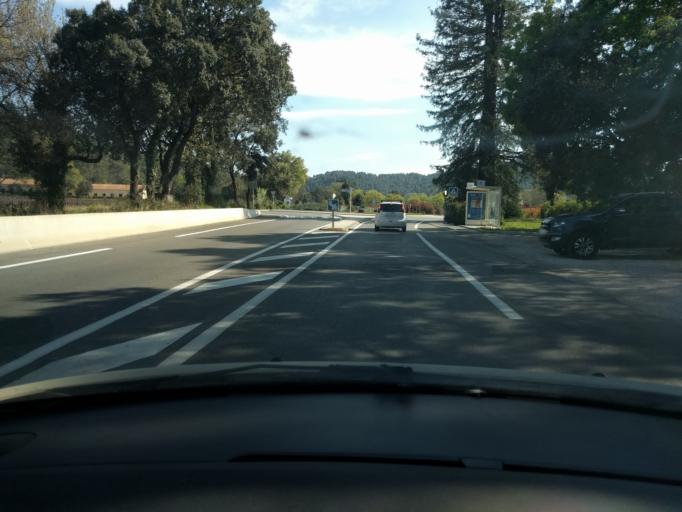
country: FR
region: Provence-Alpes-Cote d'Azur
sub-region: Departement du Var
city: La Crau
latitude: 43.1731
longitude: 6.1180
